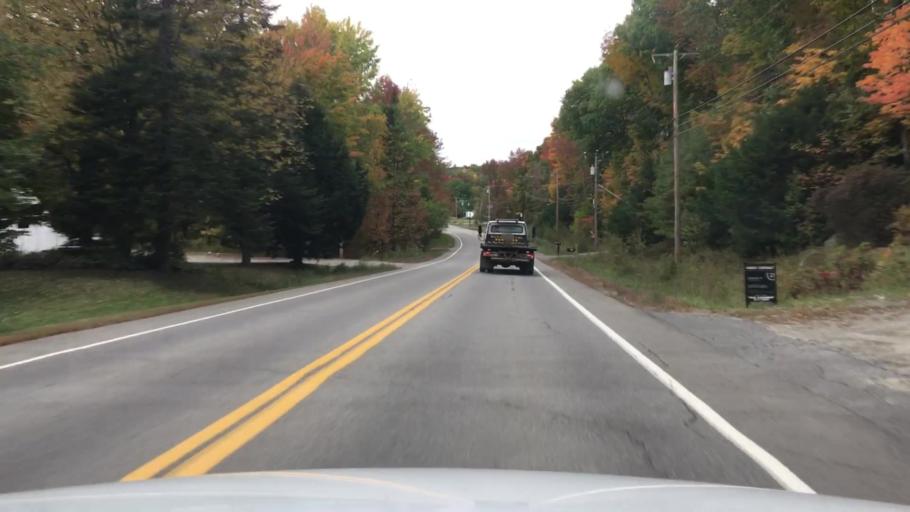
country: US
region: Maine
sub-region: Kennebec County
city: Oakland
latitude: 44.5611
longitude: -69.7448
